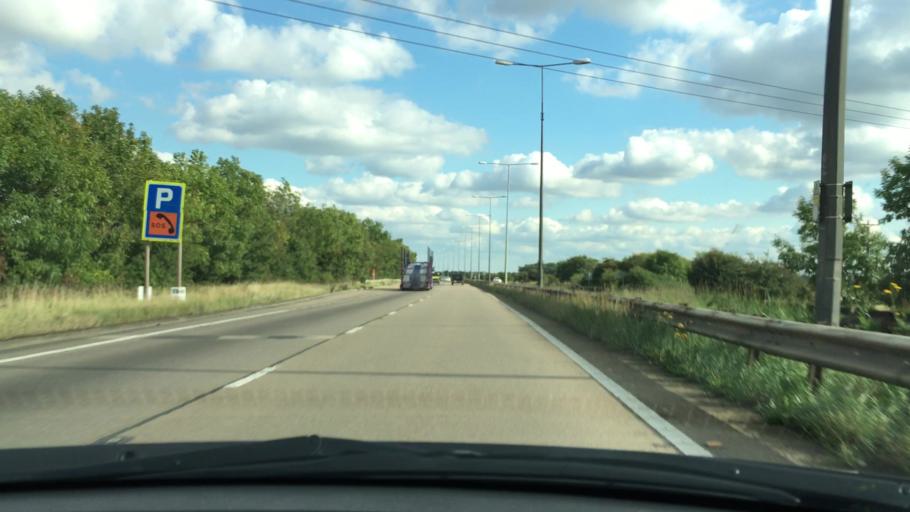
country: GB
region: England
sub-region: North East Lincolnshire
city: Healing
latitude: 53.5877
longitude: -0.1551
